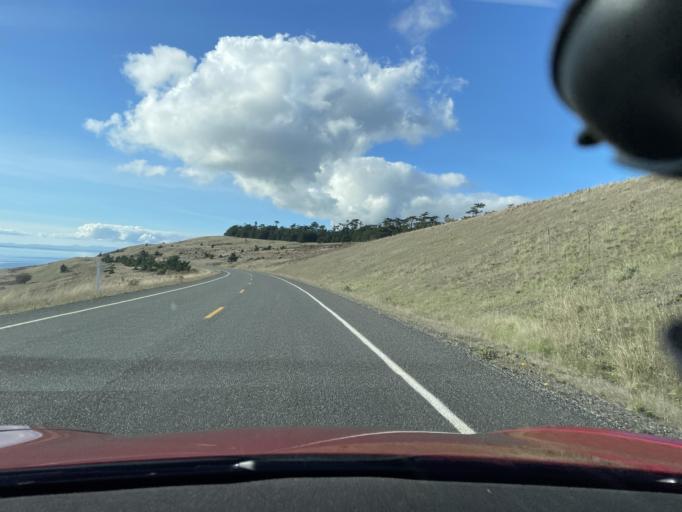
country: US
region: Washington
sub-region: San Juan County
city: Friday Harbor
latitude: 48.4568
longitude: -122.9811
